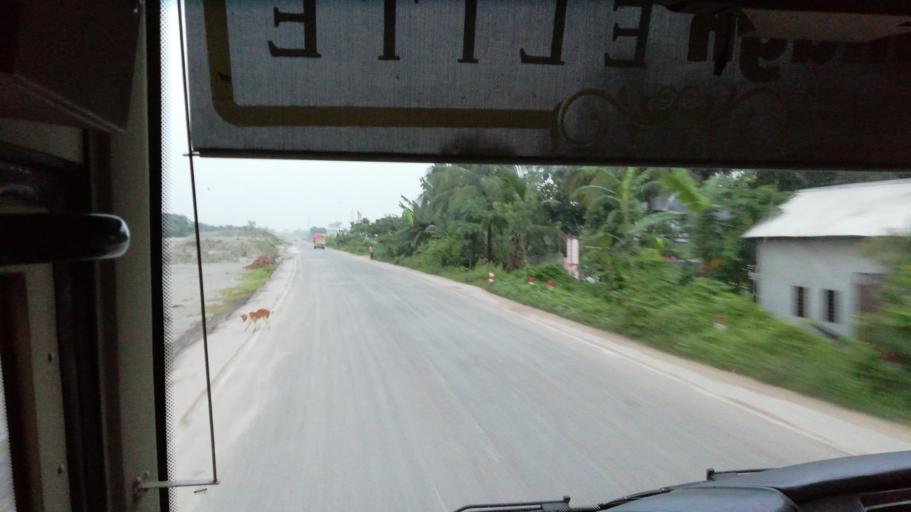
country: BD
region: Dhaka
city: Char Bhadrasan
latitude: 23.4033
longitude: 90.1485
